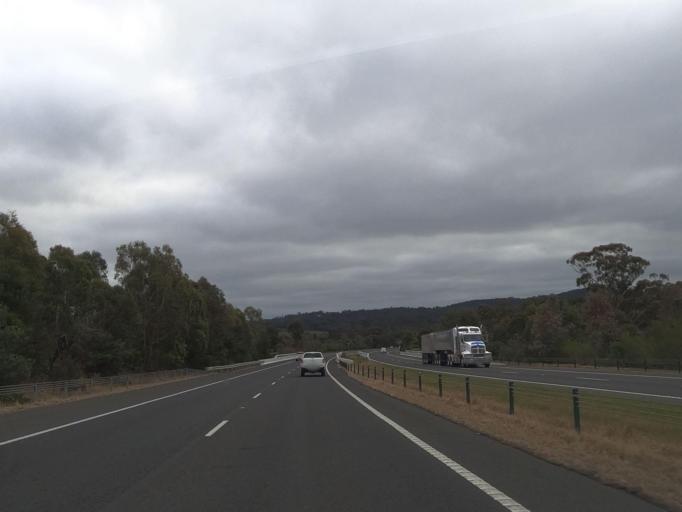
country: AU
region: Victoria
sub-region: Mount Alexander
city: Castlemaine
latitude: -37.0142
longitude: 144.2559
